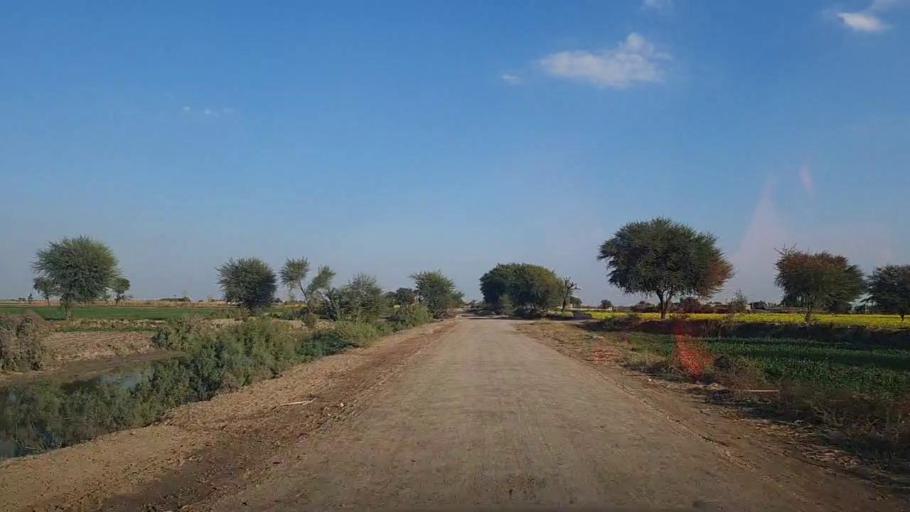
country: PK
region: Sindh
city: Jhol
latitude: 25.9212
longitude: 69.0354
